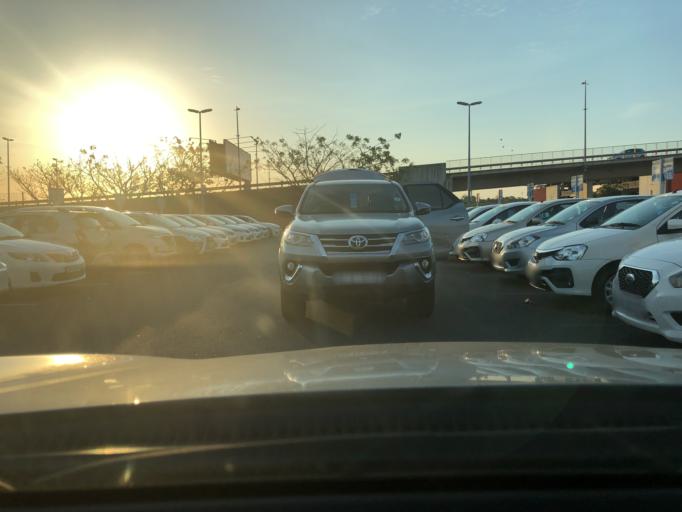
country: ZA
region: KwaZulu-Natal
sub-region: iLembe District Municipality
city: Ballitoville
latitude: -29.6213
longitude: 31.1027
